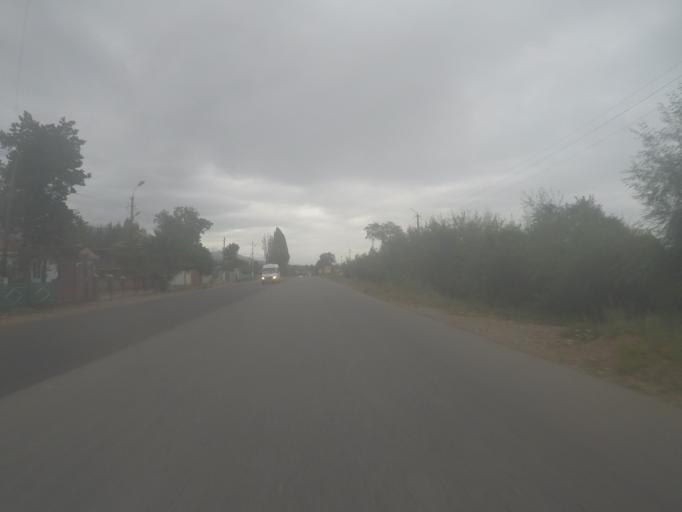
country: KG
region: Ysyk-Koel
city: Cholpon-Ata
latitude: 42.6870
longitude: 77.3443
